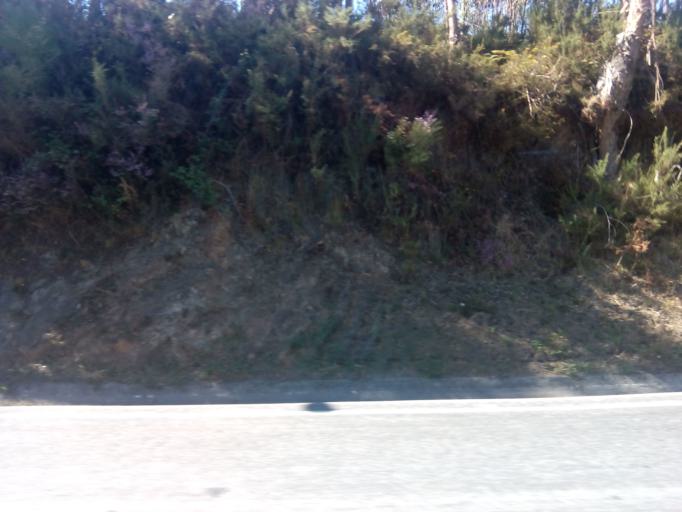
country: PT
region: Porto
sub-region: Paredes
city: Gandra
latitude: 41.1916
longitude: -8.4355
